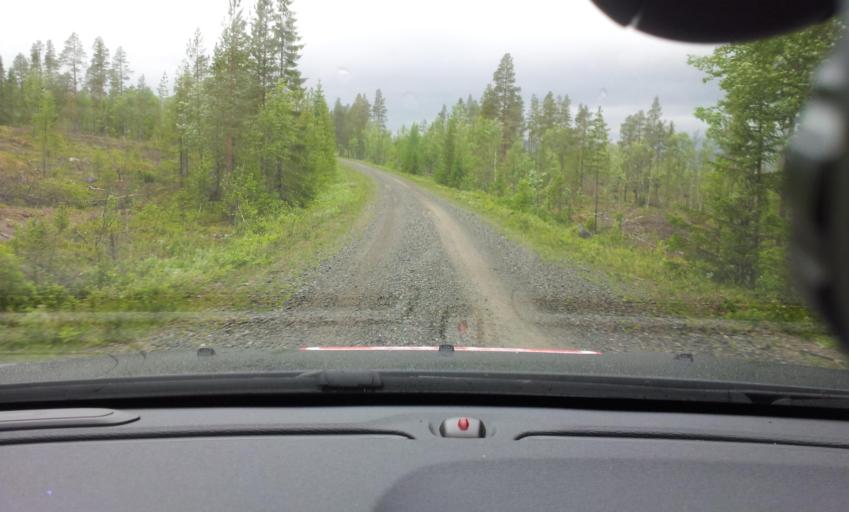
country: SE
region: Jaemtland
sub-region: Are Kommun
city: Jarpen
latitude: 63.2086
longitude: 13.3338
